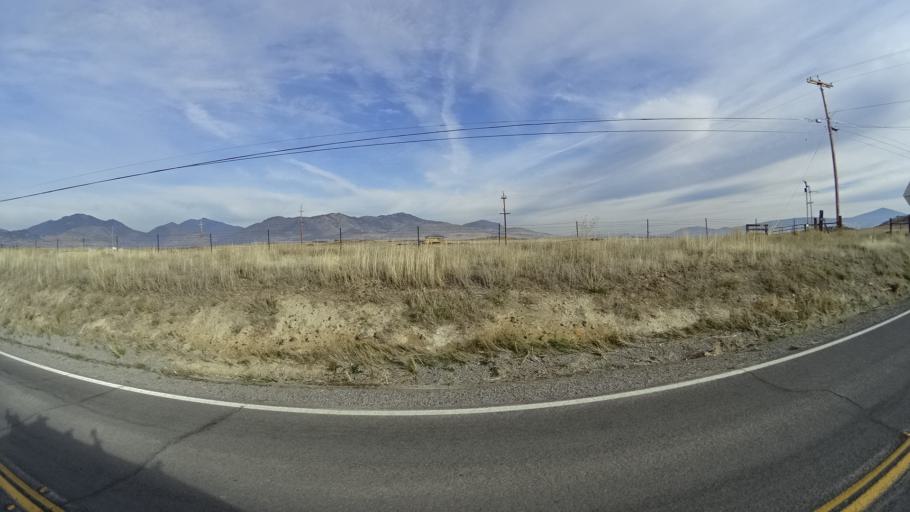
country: US
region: California
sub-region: Siskiyou County
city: Montague
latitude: 41.7253
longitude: -122.5533
